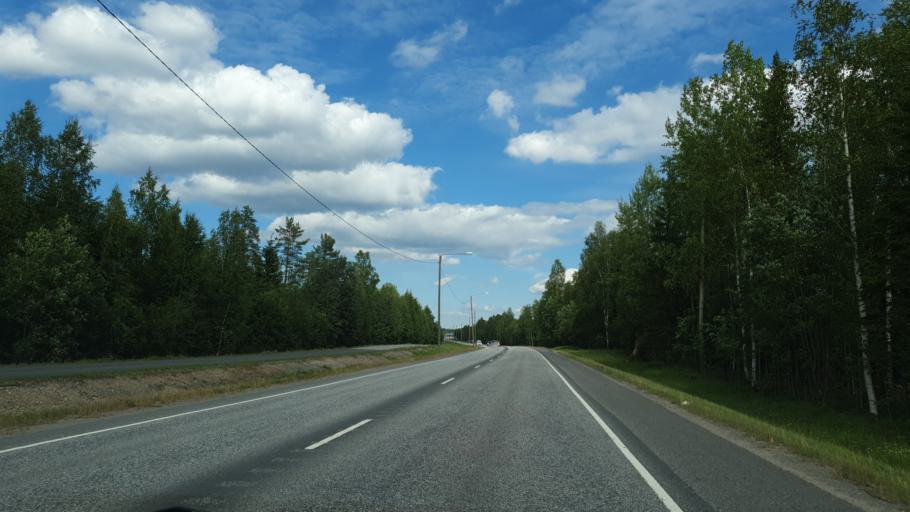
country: FI
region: Kainuu
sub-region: Kajaani
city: Kajaani
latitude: 64.2612
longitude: 27.8349
